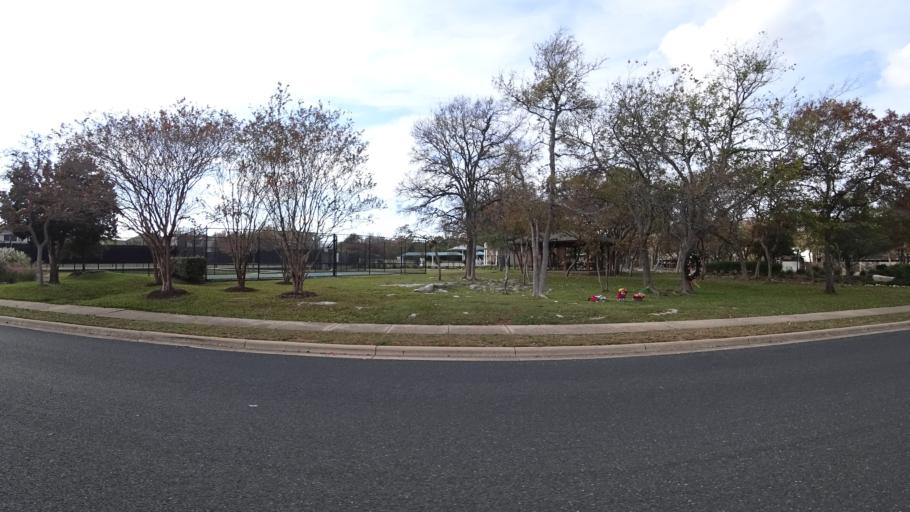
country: US
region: Texas
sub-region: Williamson County
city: Brushy Creek
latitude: 30.5105
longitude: -97.7428
